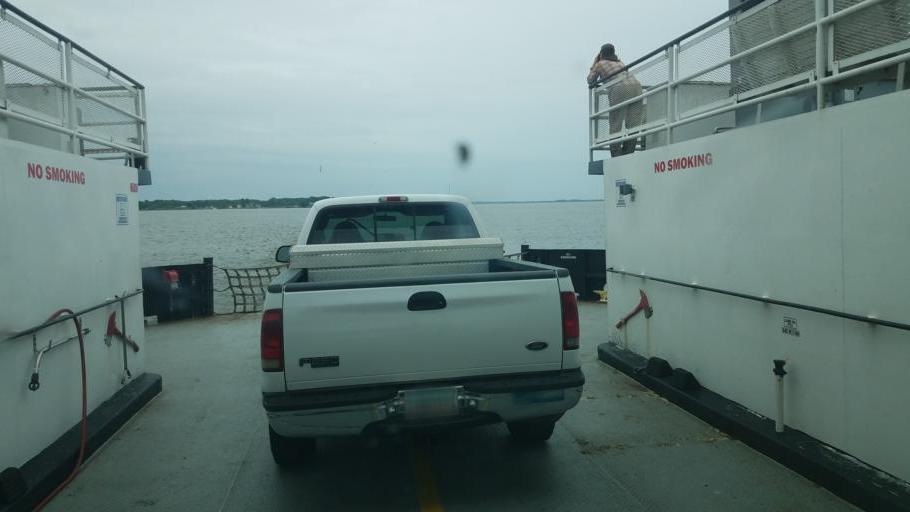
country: US
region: North Carolina
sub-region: Currituck County
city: Currituck
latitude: 36.4766
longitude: -75.9406
